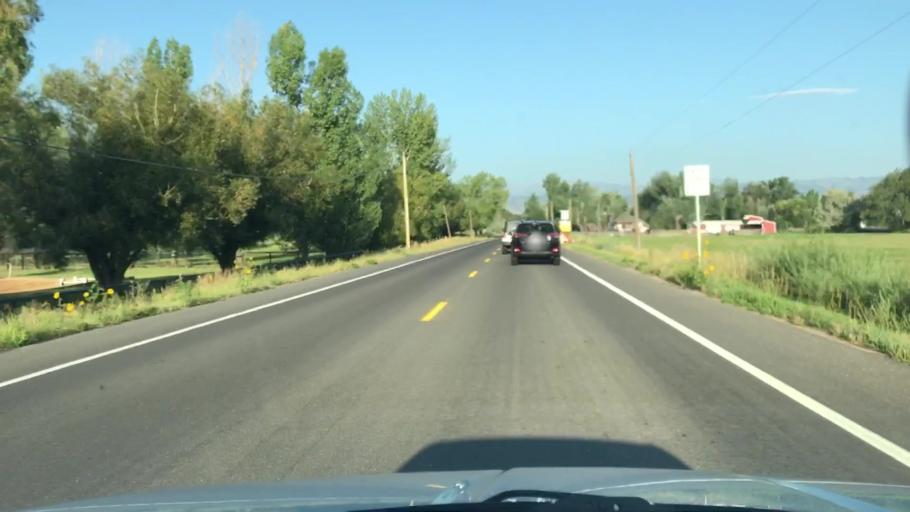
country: US
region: Colorado
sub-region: Boulder County
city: Gunbarrel
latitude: 40.0365
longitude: -105.1599
